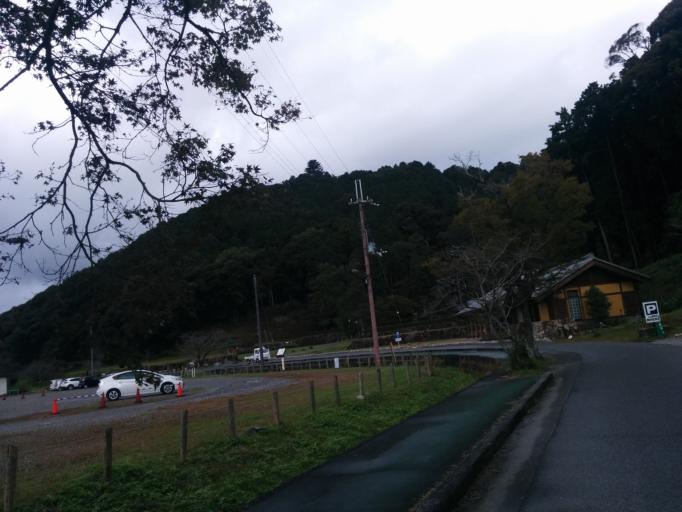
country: JP
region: Shiga Prefecture
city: Omihachiman
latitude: 35.1523
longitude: 136.1400
